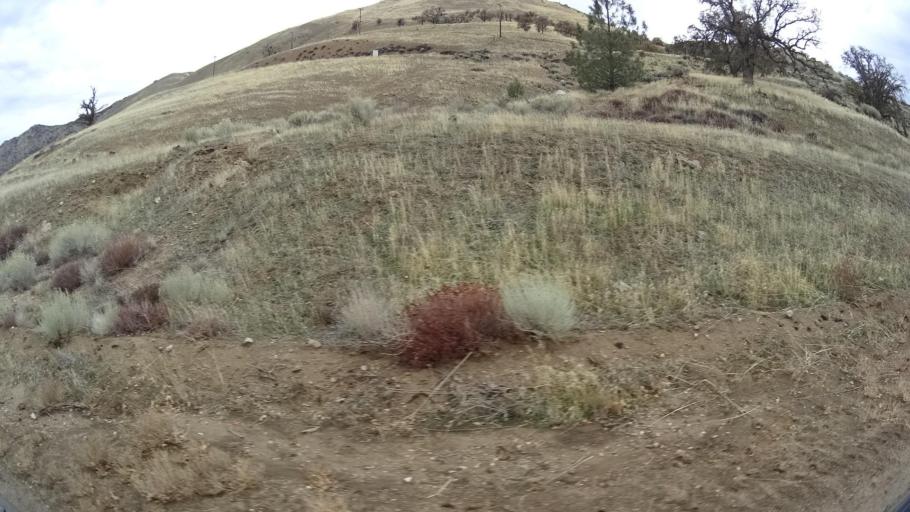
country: US
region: California
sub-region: Kern County
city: Golden Hills
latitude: 35.1336
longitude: -118.5582
